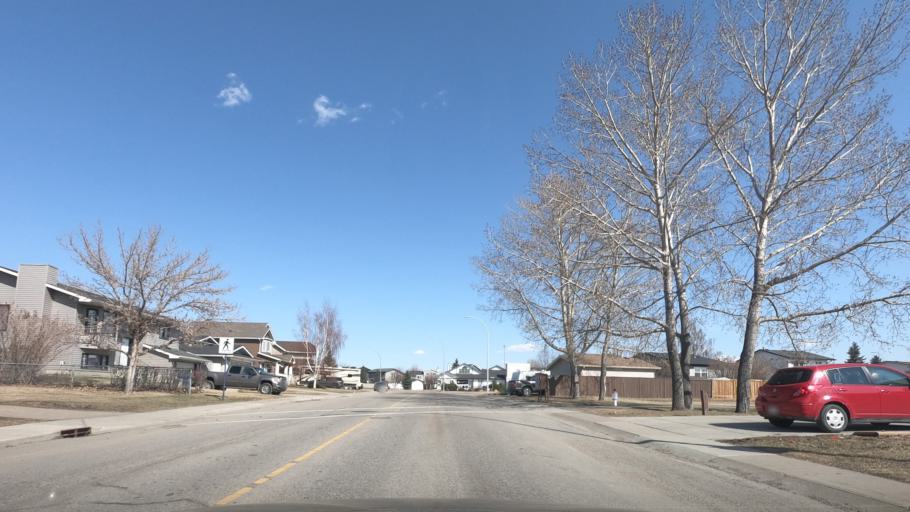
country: CA
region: Alberta
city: Airdrie
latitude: 51.2794
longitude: -114.0072
